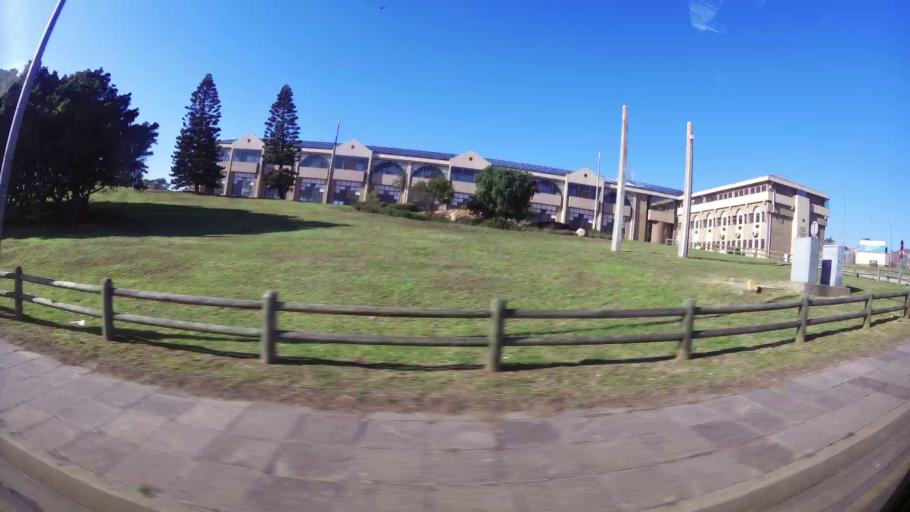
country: ZA
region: Eastern Cape
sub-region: Nelson Mandela Bay Metropolitan Municipality
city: Port Elizabeth
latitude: -33.9694
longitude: 25.6275
